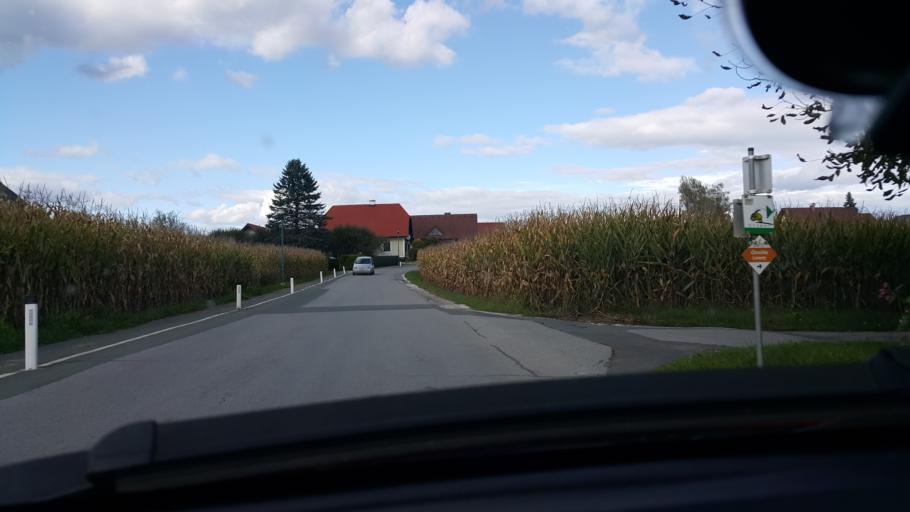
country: AT
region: Styria
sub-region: Politischer Bezirk Deutschlandsberg
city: Sankt Martin im Sulmtal
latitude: 46.7550
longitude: 15.2890
